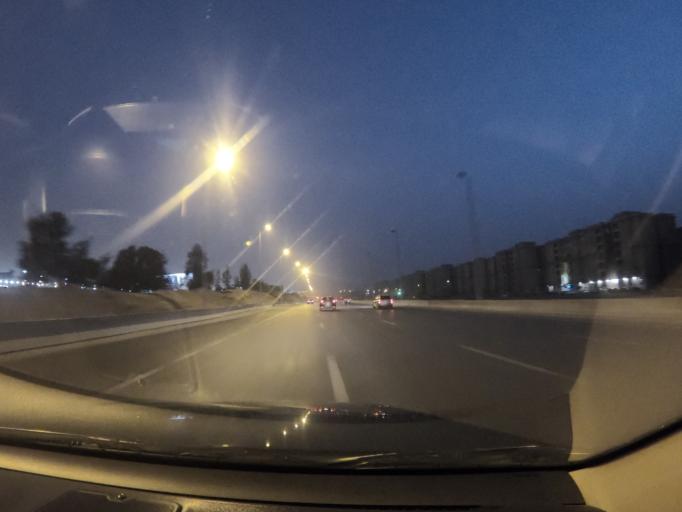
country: EG
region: Muhafazat al Qahirah
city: Cairo
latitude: 30.0416
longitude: 31.4035
